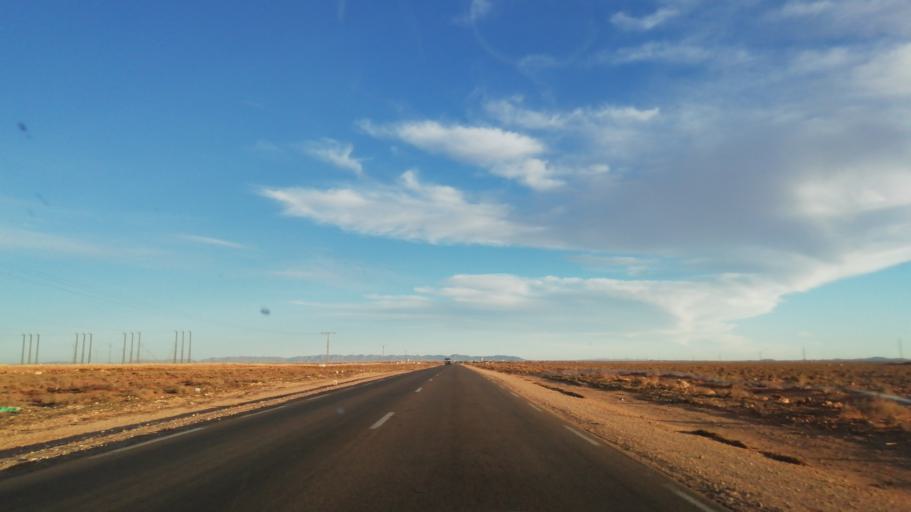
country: DZ
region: Wilaya de Naama
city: Naama
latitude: 33.7358
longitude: -0.7627
